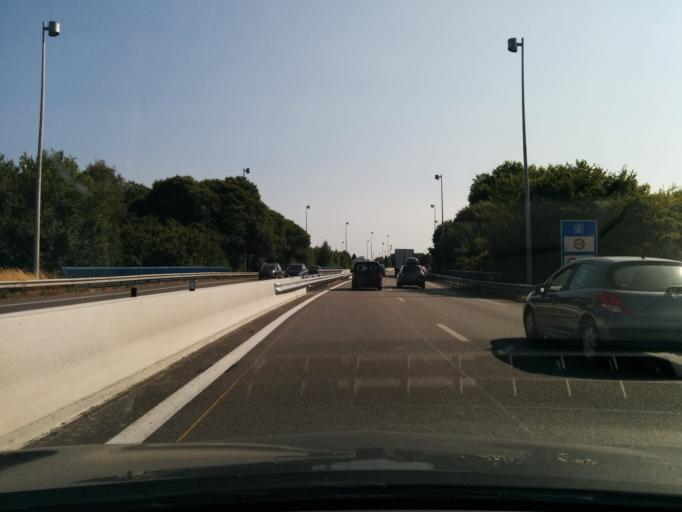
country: FR
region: Limousin
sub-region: Departement de la Haute-Vienne
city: Rilhac-Rancon
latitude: 45.8833
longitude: 1.2910
